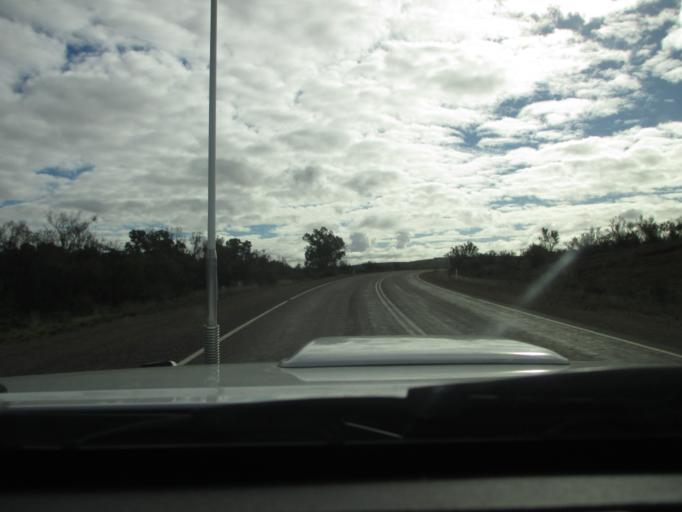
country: AU
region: South Australia
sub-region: Flinders Ranges
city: Quorn
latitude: -32.3302
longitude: 138.4742
